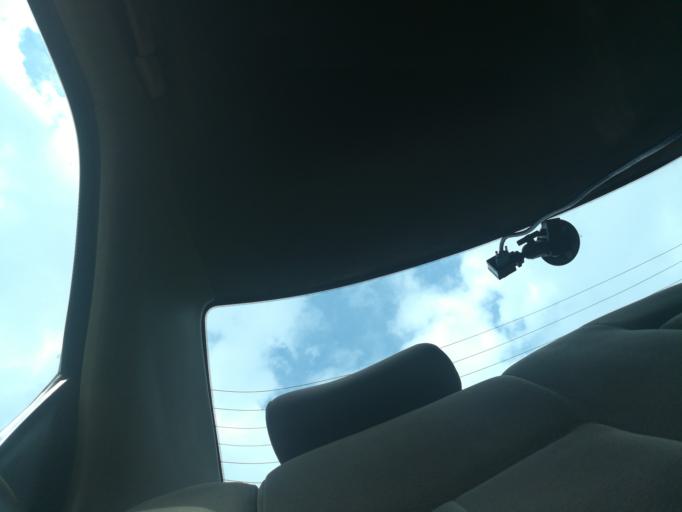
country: NG
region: Lagos
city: Ikorodu
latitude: 6.6627
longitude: 3.5967
